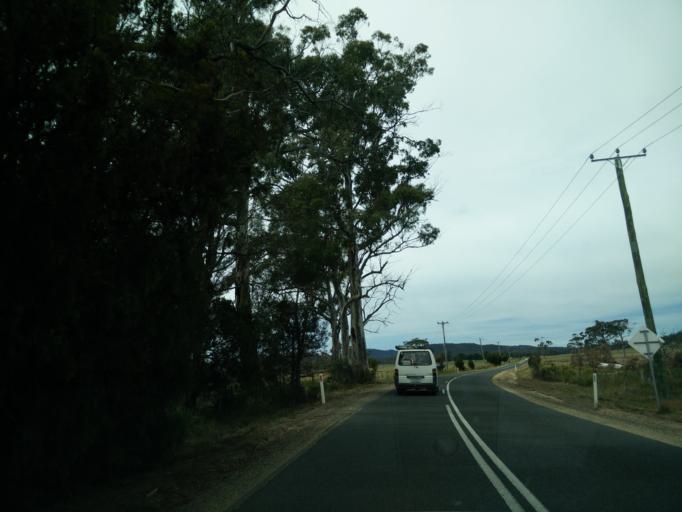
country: AU
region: Tasmania
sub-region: Break O'Day
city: St Helens
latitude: -41.8993
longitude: 148.2550
